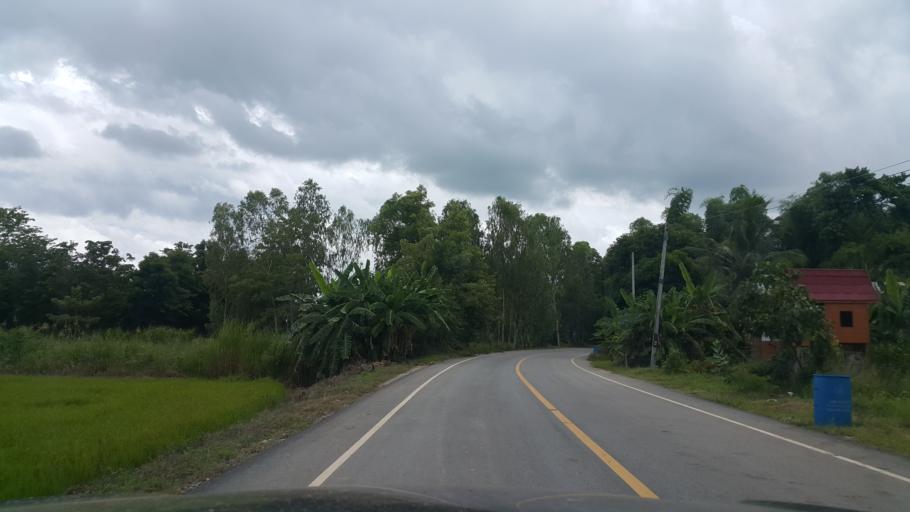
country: TH
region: Sukhothai
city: Kong Krailat
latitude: 16.9097
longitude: 99.8858
